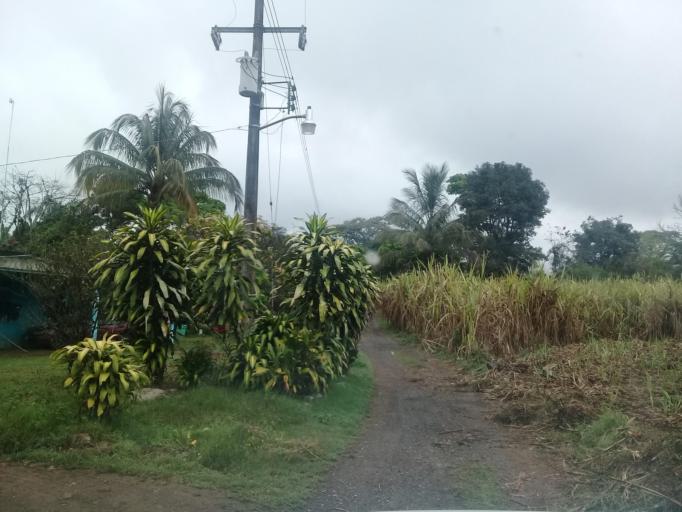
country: MX
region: Veracruz
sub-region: Amatlan de los Reyes
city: Trapiche Viejo
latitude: 18.8282
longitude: -96.9571
